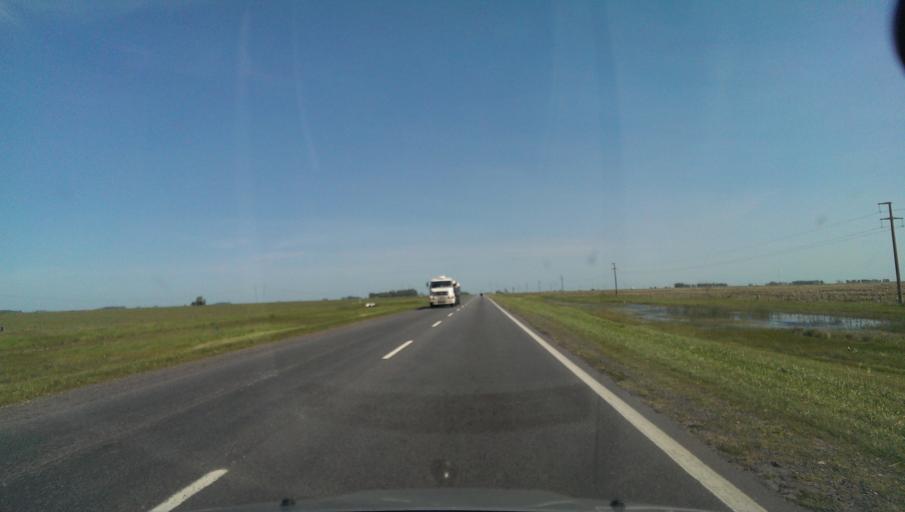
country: AR
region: Buenos Aires
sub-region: Partido de Azul
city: Azul
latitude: -36.5752
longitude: -59.6429
